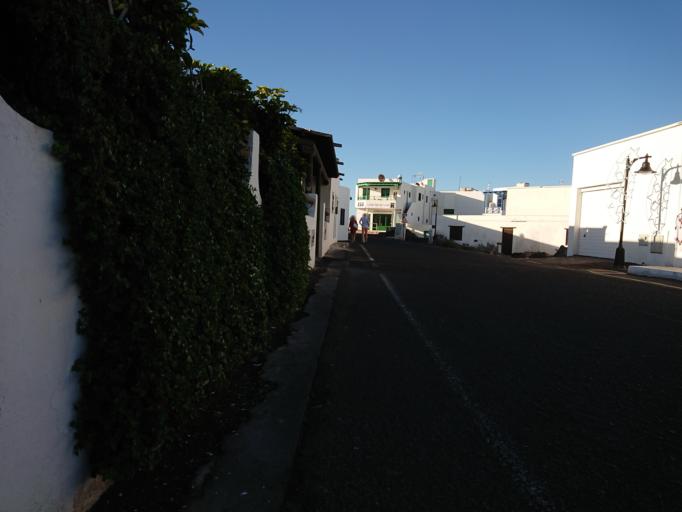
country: ES
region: Canary Islands
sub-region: Provincia de Las Palmas
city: Yaiza
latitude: 28.9817
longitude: -13.8311
